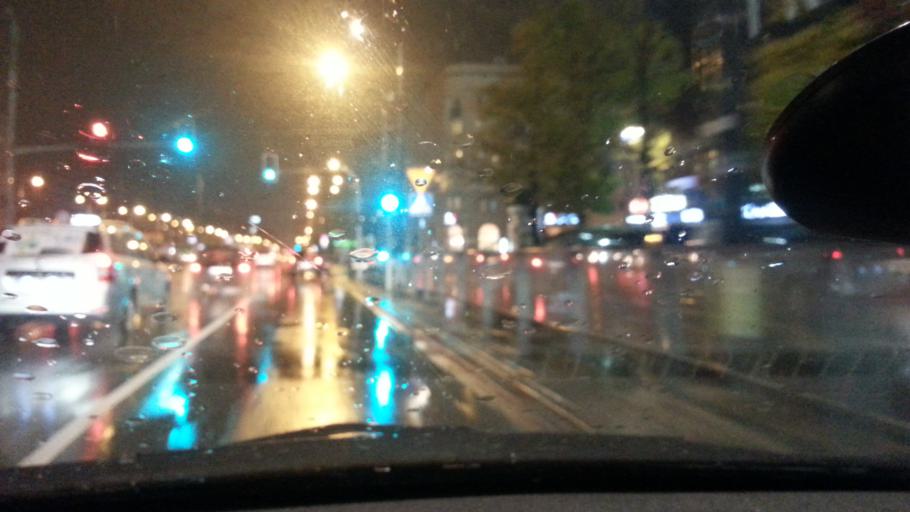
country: PL
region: Masovian Voivodeship
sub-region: Warszawa
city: Wola
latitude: 52.2415
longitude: 20.9943
